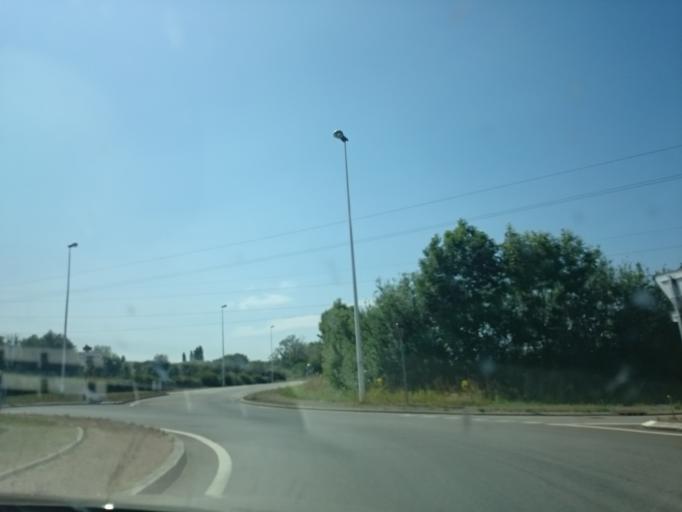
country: FR
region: Pays de la Loire
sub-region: Departement de la Loire-Atlantique
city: Indre
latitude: 47.2073
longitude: -1.6838
